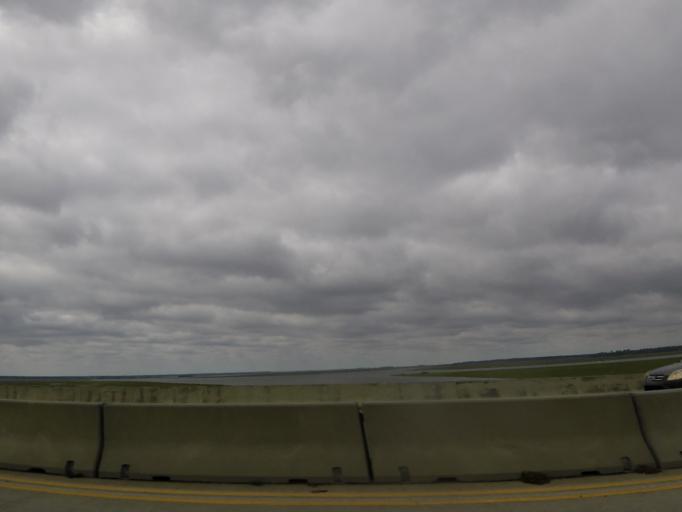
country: US
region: Georgia
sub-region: Glynn County
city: Saint Simon Mills
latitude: 31.1712
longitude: -81.4245
